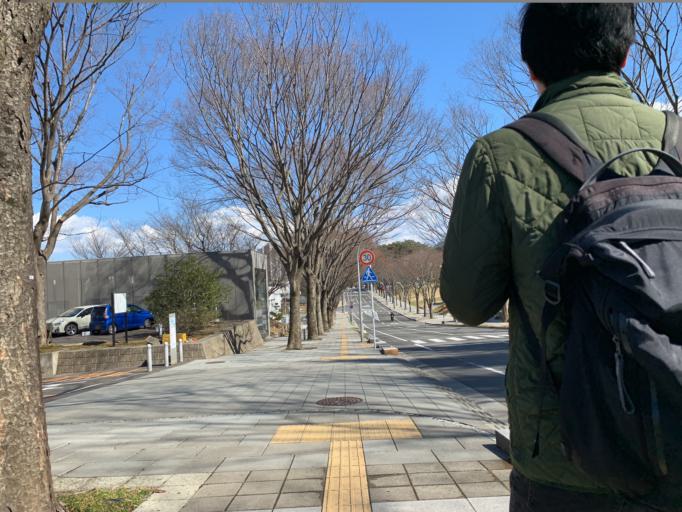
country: JP
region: Miyagi
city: Sendai
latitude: 38.2552
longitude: 140.8402
